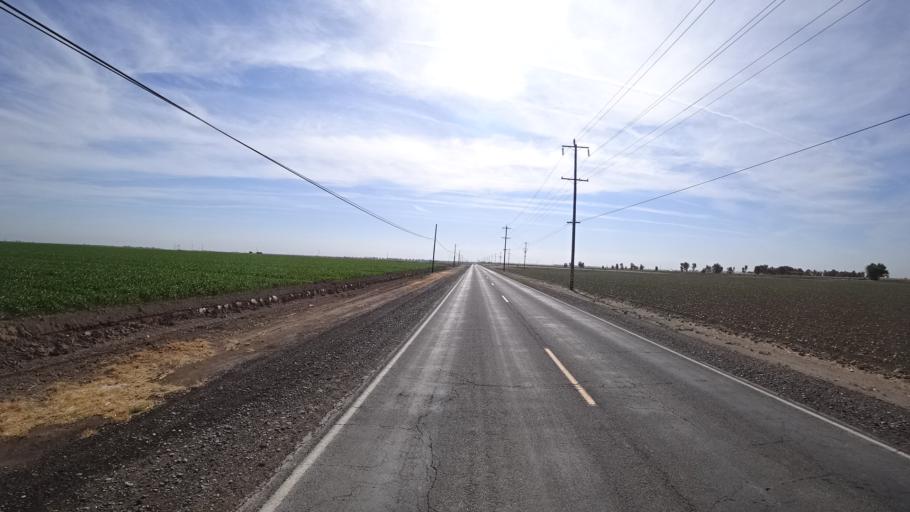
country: US
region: California
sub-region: Kings County
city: Home Garden
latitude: 36.3429
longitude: -119.5435
